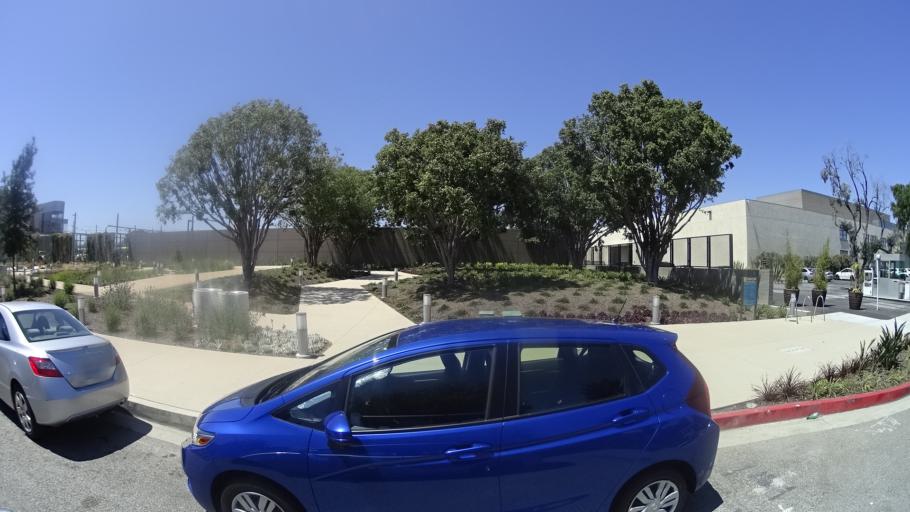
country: US
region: California
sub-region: Los Angeles County
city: Santa Monica
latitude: 34.0290
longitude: -118.4605
